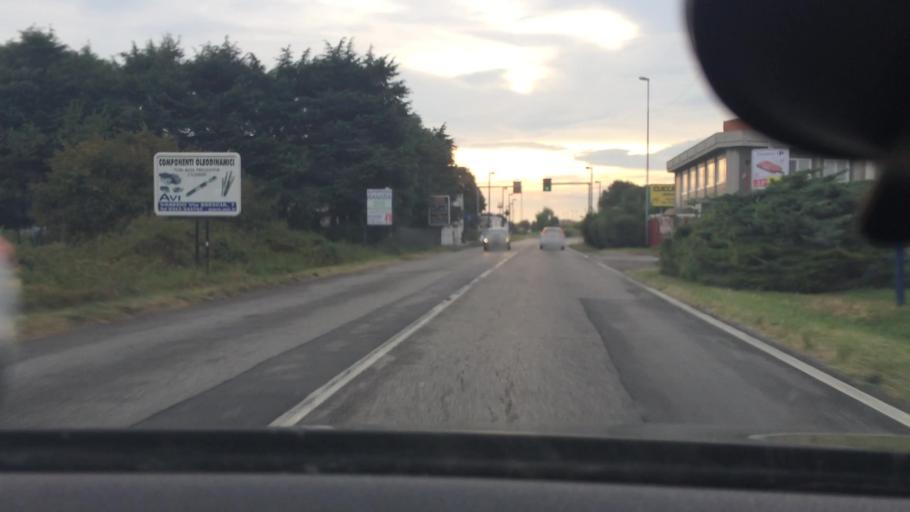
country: IT
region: Lombardy
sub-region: Provincia di Monza e Brianza
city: Varedo
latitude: 45.5956
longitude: 9.1784
